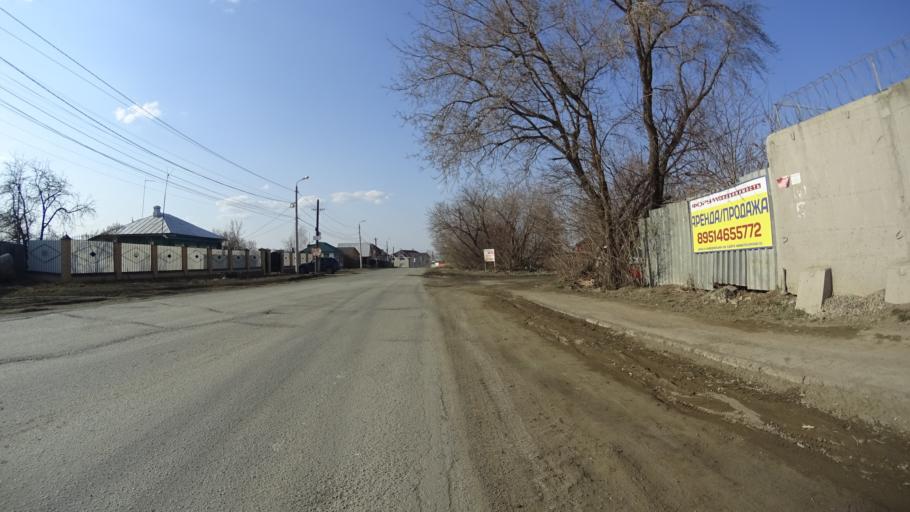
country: RU
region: Chelyabinsk
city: Novosineglazovskiy
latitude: 55.1094
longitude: 61.3336
